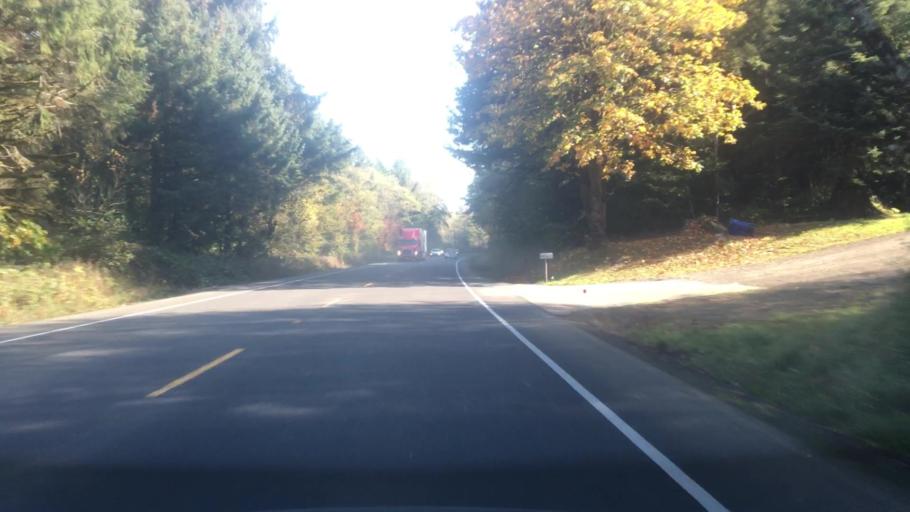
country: US
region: Oregon
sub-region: Lincoln County
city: Rose Lodge
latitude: 45.0121
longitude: -123.9269
